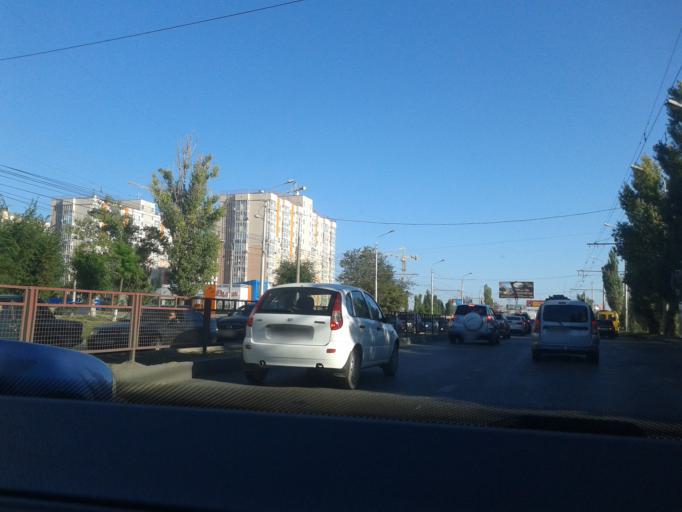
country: RU
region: Volgograd
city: Volgograd
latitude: 48.6218
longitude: 44.4250
